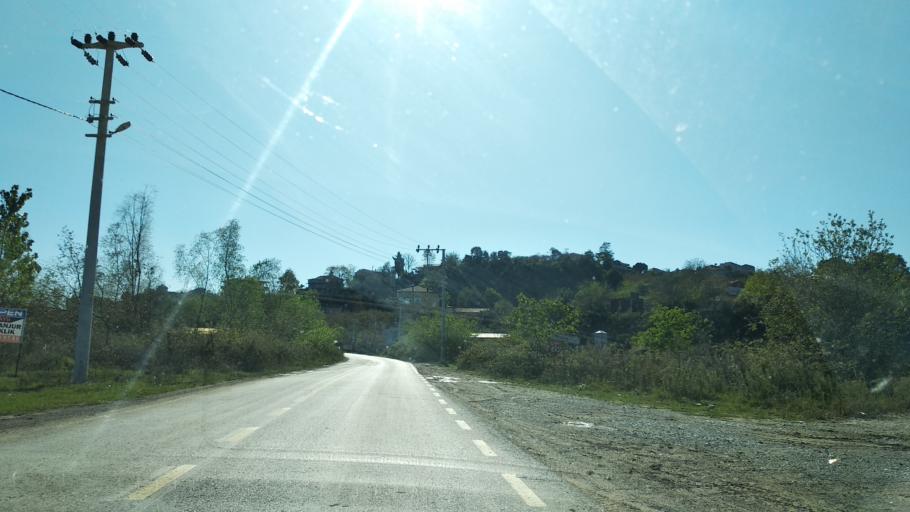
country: TR
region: Sakarya
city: Karasu
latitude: 41.1086
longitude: 30.6406
